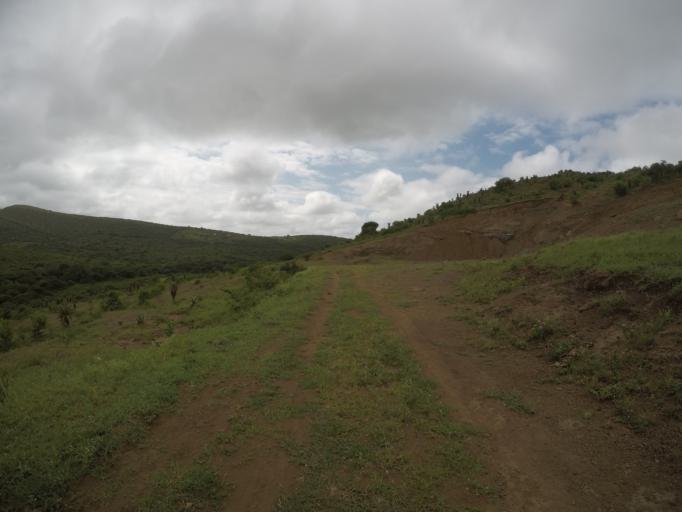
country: ZA
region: KwaZulu-Natal
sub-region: uThungulu District Municipality
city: Empangeni
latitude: -28.6271
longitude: 31.8780
